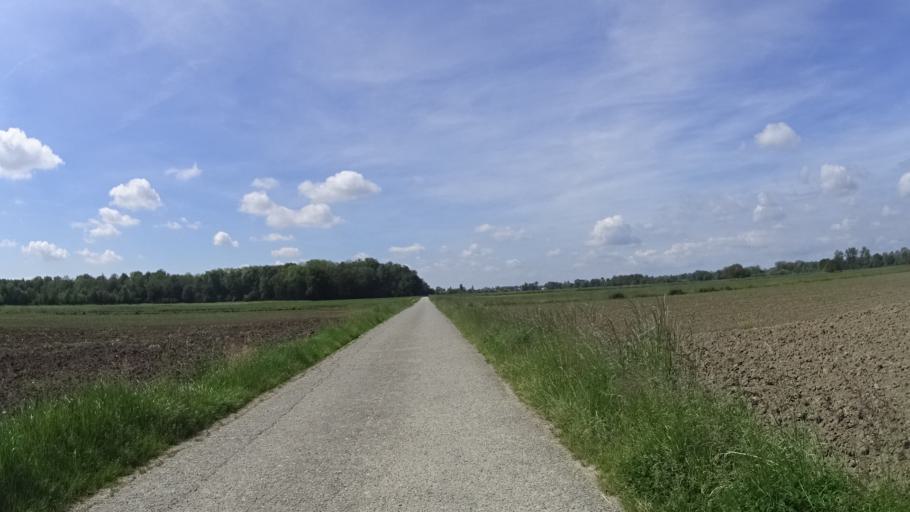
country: DE
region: Baden-Wuerttemberg
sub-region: Freiburg Region
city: Meissenheim
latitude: 48.4269
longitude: 7.7874
